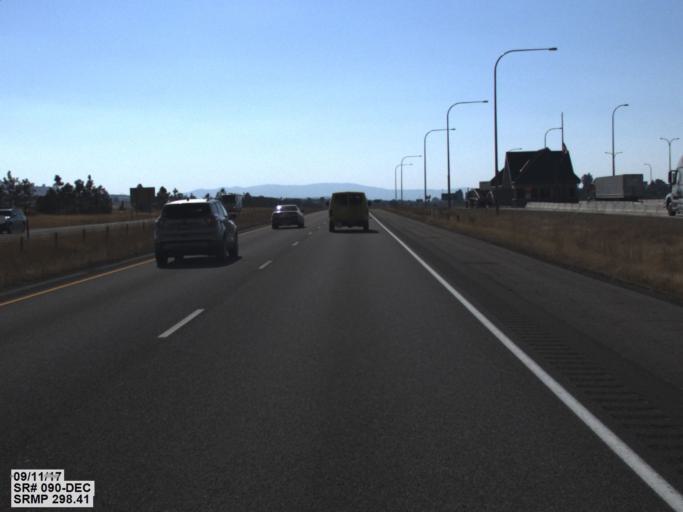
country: US
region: Washington
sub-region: Spokane County
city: Otis Orchards-East Farms
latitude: 47.6884
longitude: -117.0690
